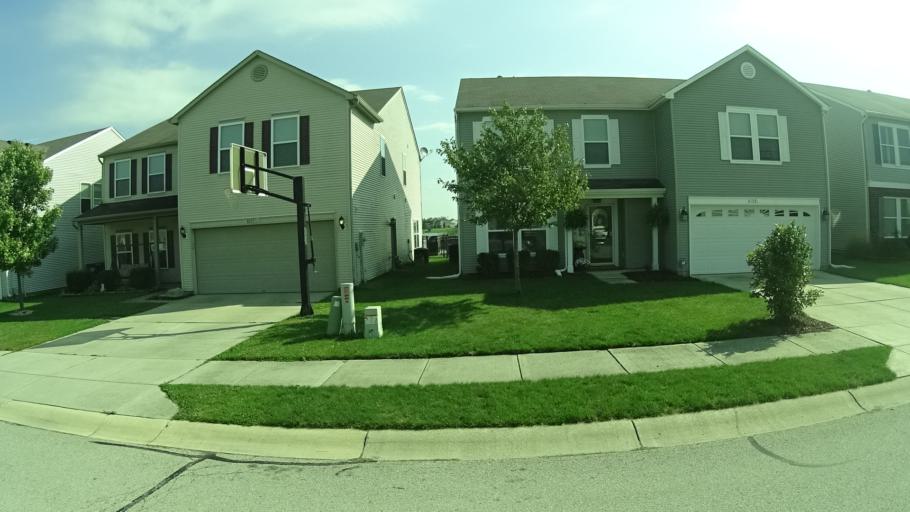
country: US
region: Indiana
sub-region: Hancock County
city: Fortville
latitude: 39.9855
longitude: -85.8550
